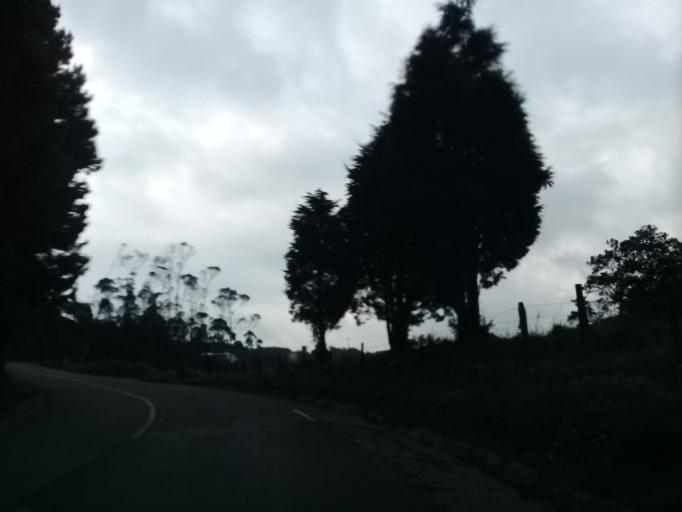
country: CO
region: Cundinamarca
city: Cogua
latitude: 5.0869
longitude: -74.0601
